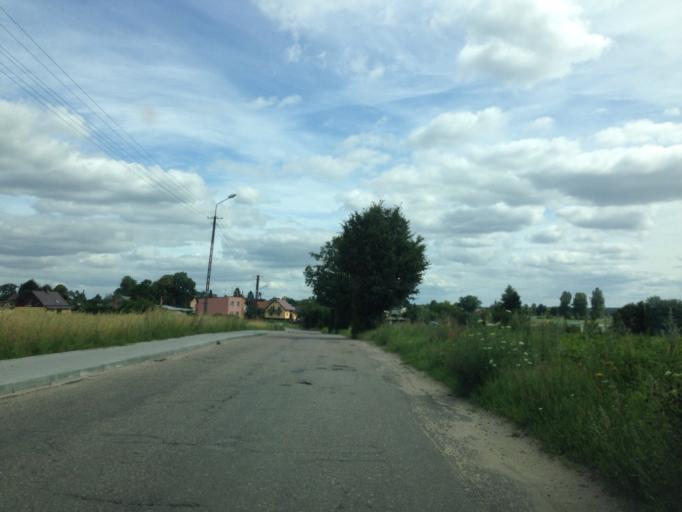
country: PL
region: Pomeranian Voivodeship
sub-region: Powiat koscierski
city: Lipusz
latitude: 54.0931
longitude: 17.7772
